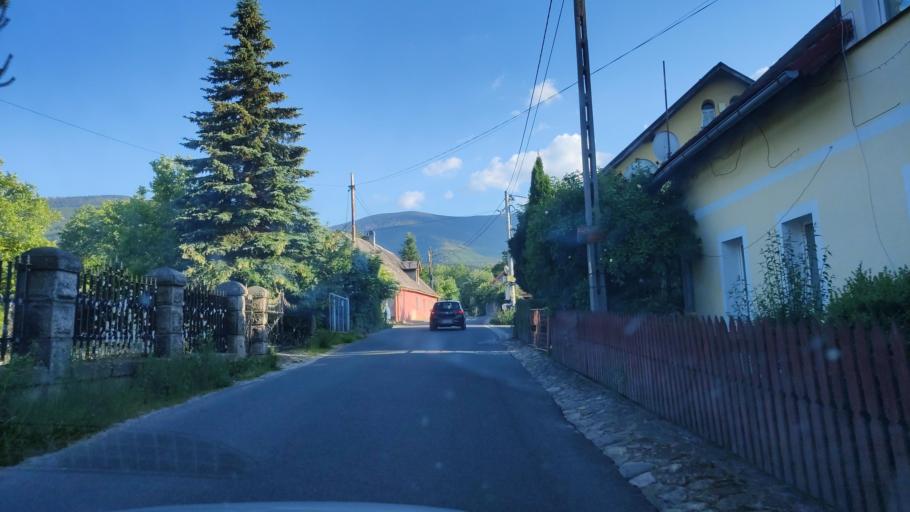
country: PL
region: Lower Silesian Voivodeship
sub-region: Powiat jeleniogorski
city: Karpacz
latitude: 50.7859
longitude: 15.7783
